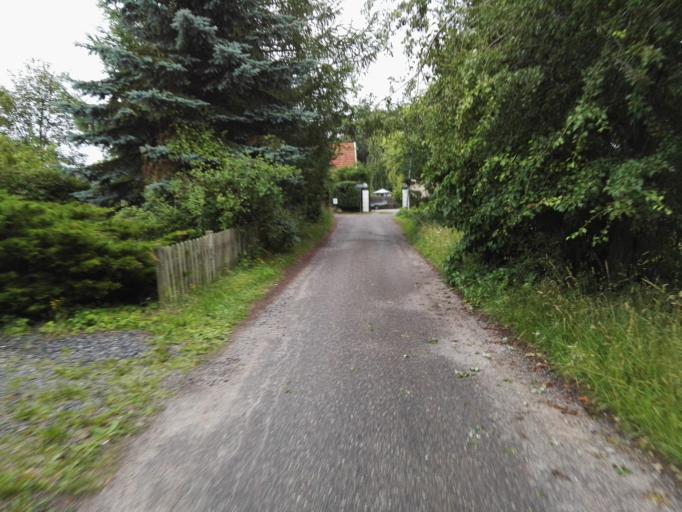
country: DK
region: Capital Region
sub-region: Egedal Kommune
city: Smorumnedre
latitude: 55.7389
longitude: 12.3167
